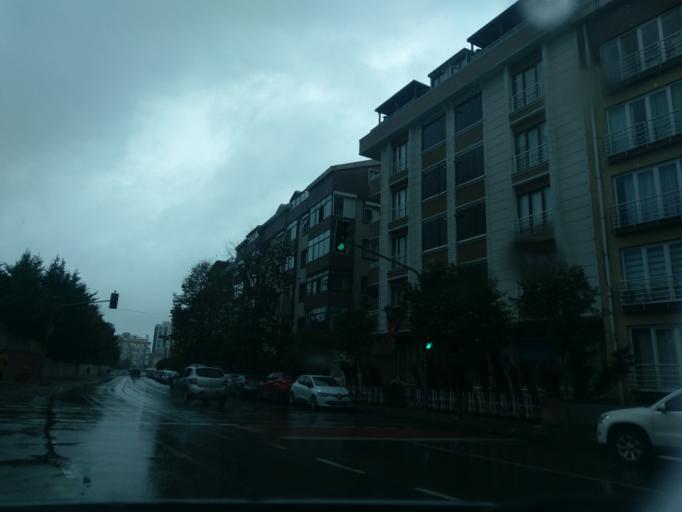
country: TR
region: Istanbul
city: Sisli
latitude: 41.0858
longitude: 28.9646
